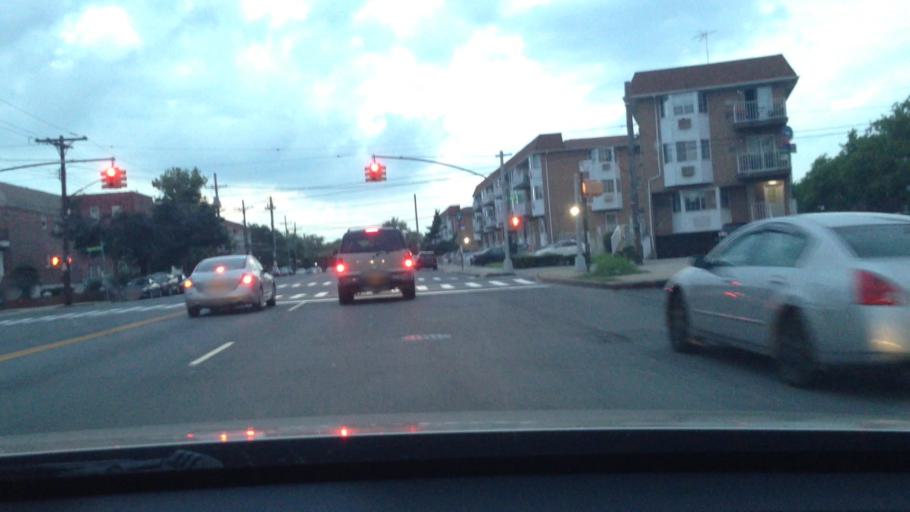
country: US
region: New York
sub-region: Kings County
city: East New York
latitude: 40.6296
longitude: -73.9043
